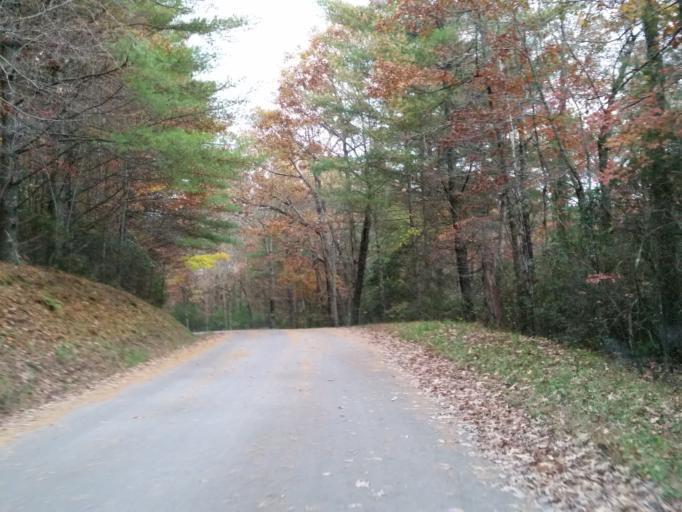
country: US
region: Georgia
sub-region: Fannin County
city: Blue Ridge
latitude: 34.7274
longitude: -84.2048
